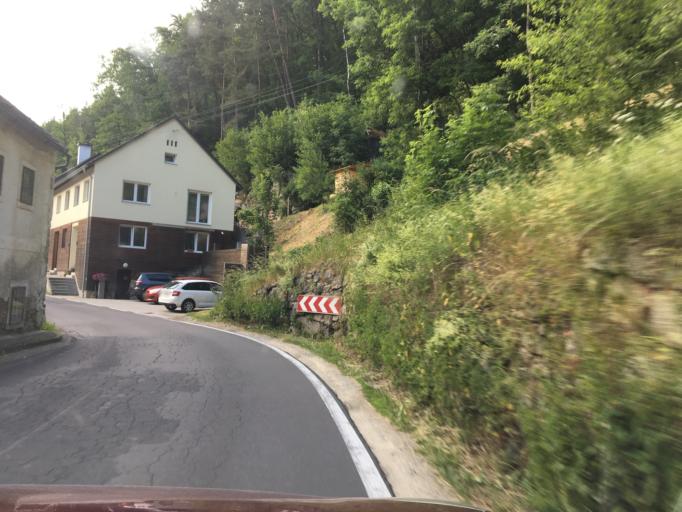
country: AT
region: Upper Austria
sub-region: Politischer Bezirk Urfahr-Umgebung
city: Alberndorf in der Riedmark
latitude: 48.4064
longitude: 14.4000
